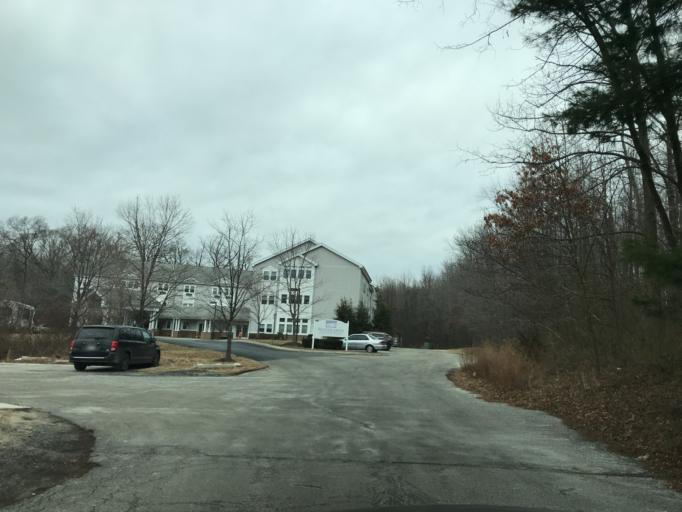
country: US
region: Maryland
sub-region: Baltimore County
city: Middle River
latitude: 39.3368
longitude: -76.4504
